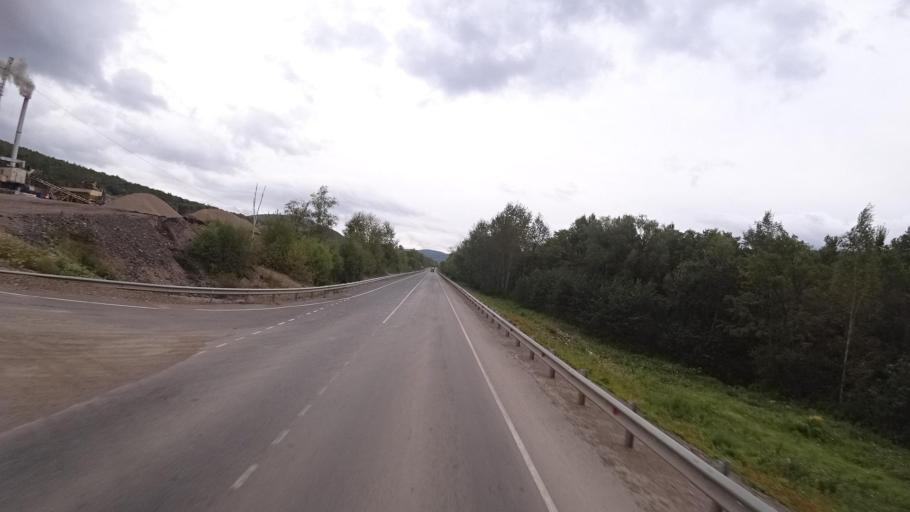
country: RU
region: Jewish Autonomous Oblast
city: Khingansk
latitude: 48.9897
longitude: 131.1251
